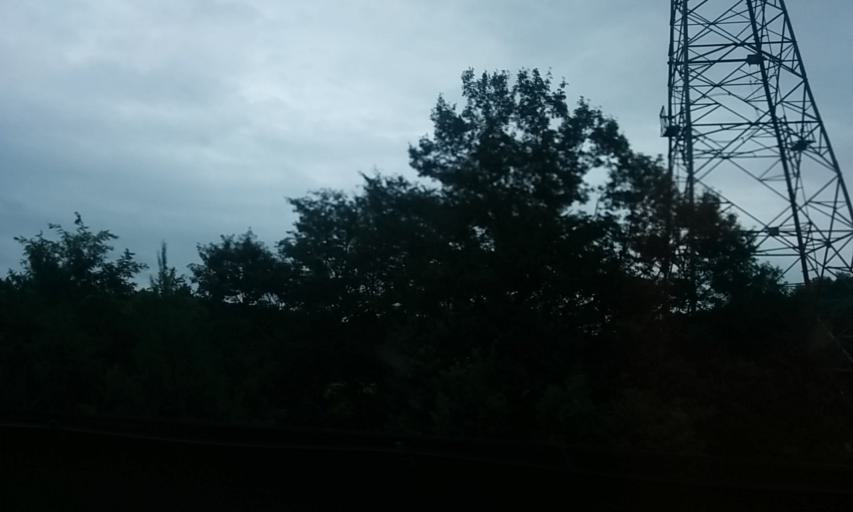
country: JP
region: Tochigi
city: Yaita
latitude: 36.7891
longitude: 139.9539
